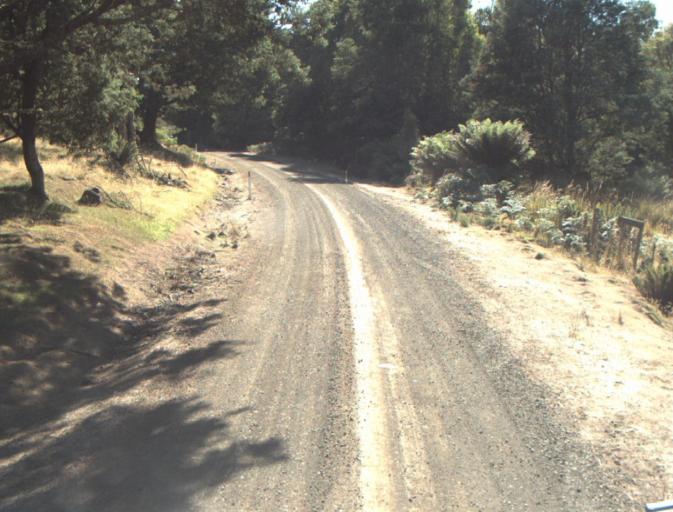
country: AU
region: Tasmania
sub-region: Dorset
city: Scottsdale
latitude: -41.2916
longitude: 147.3562
